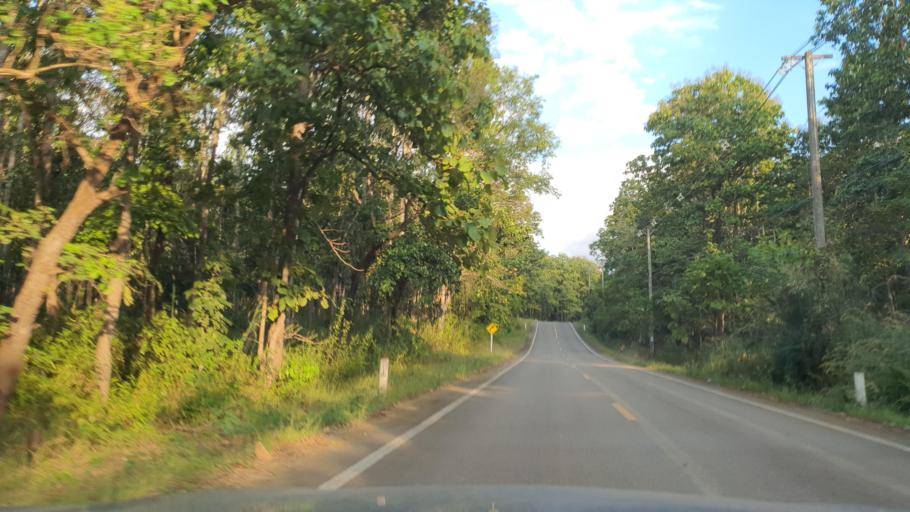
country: TH
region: Chiang Mai
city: Mae On
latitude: 18.8548
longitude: 99.2502
